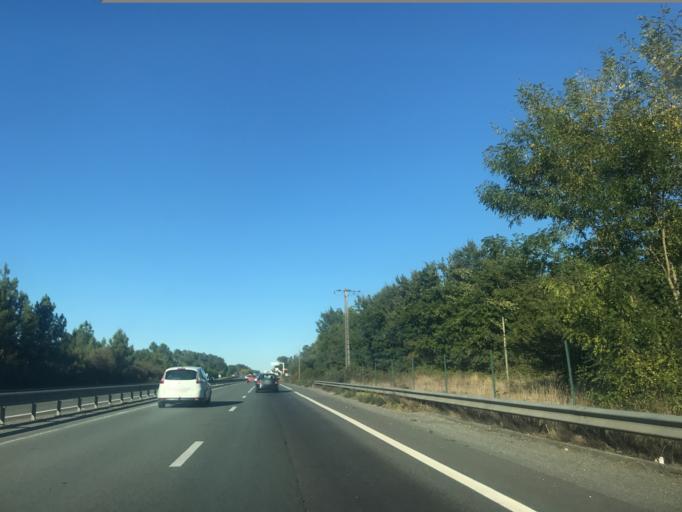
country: FR
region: Aquitaine
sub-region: Departement de la Gironde
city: Laruscade
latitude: 45.1656
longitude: -0.3400
